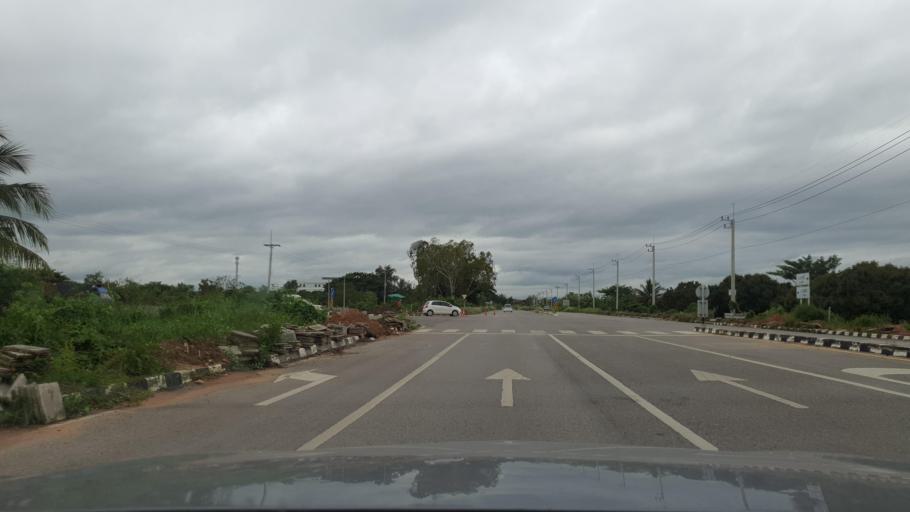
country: TH
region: Lamphun
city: Lamphun
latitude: 18.6081
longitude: 99.0134
